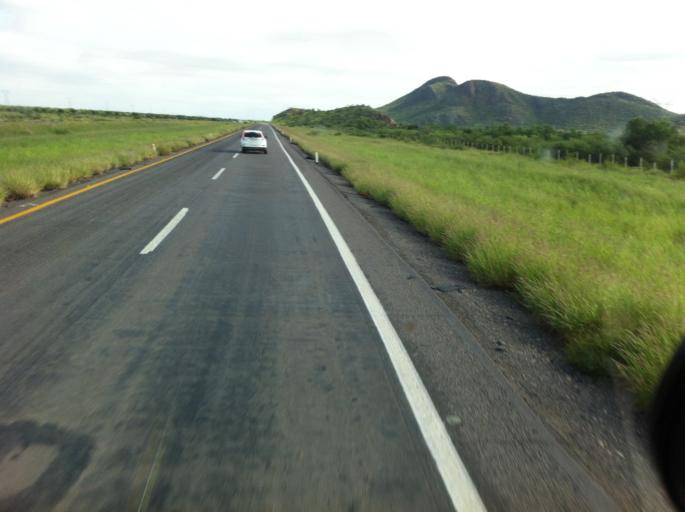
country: MX
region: Sonora
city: Hermosillo
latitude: 28.6193
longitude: -111.0147
